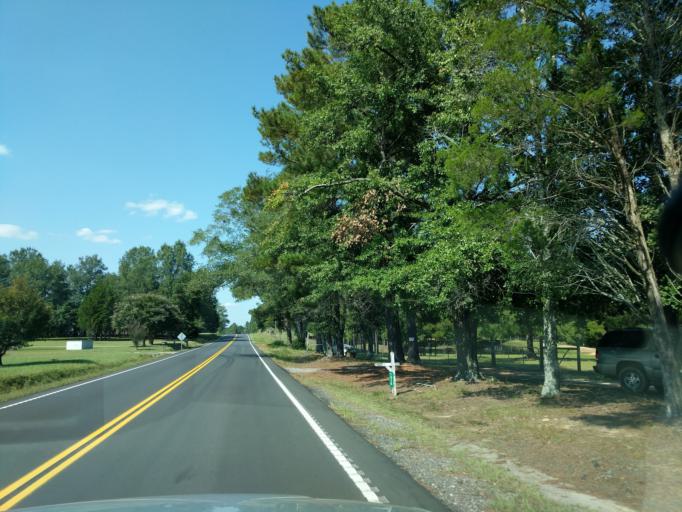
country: US
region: South Carolina
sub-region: Lexington County
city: Batesburg-Leesville
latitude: 33.9410
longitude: -81.5349
